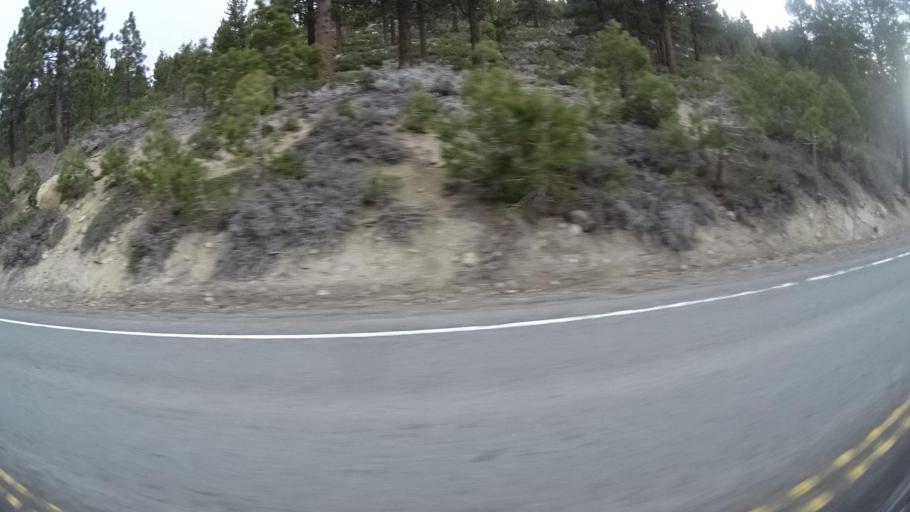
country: US
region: Nevada
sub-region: Washoe County
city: Incline Village
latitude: 39.3390
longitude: -119.8586
